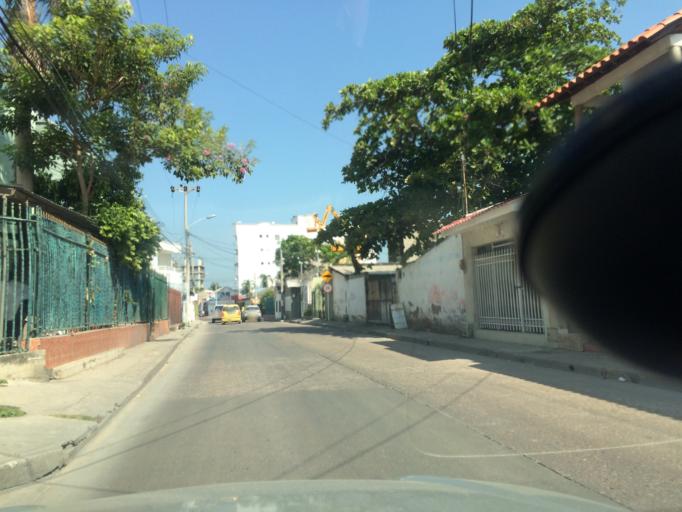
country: CO
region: Bolivar
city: Cartagena
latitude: 10.4170
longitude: -75.5373
